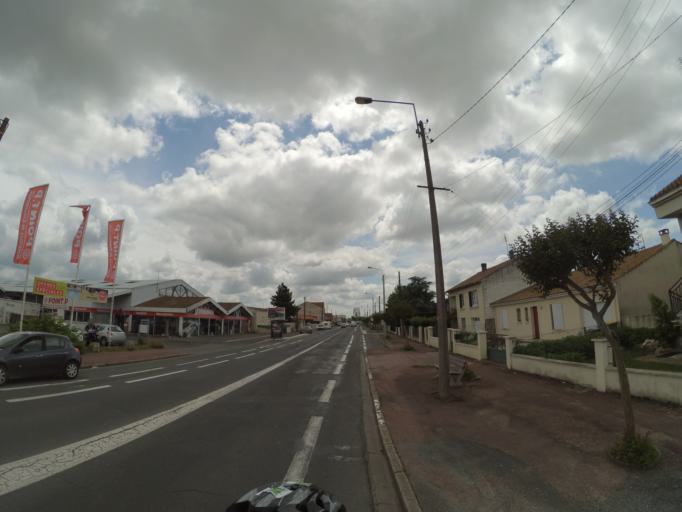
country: FR
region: Poitou-Charentes
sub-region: Departement de la Charente-Maritime
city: Rochefort
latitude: 45.9295
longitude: -0.9597
